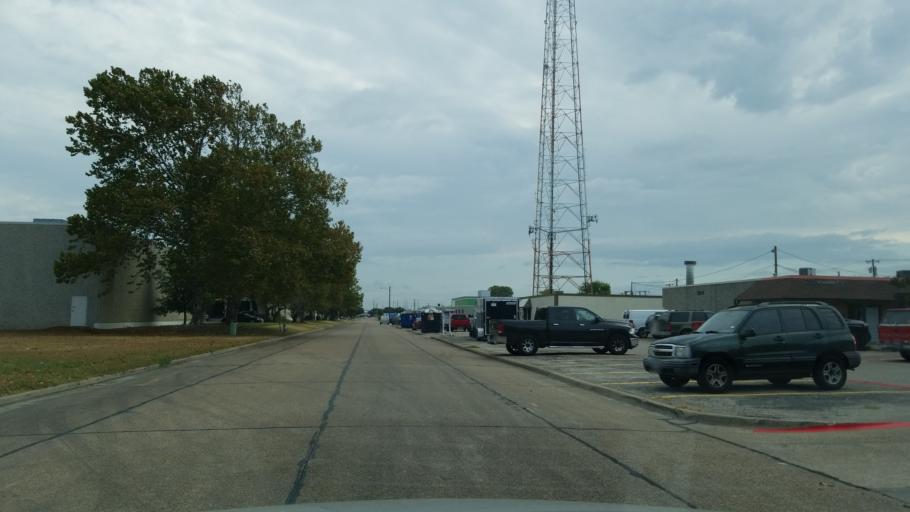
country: US
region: Texas
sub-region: Dallas County
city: Garland
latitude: 32.9018
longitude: -96.6896
